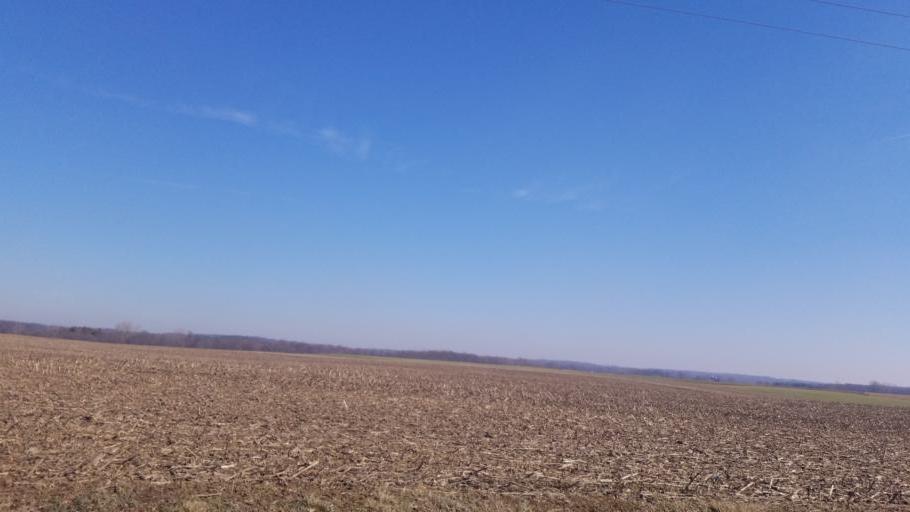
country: US
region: Ohio
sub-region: Richland County
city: Shelby
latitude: 40.9186
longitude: -82.5738
